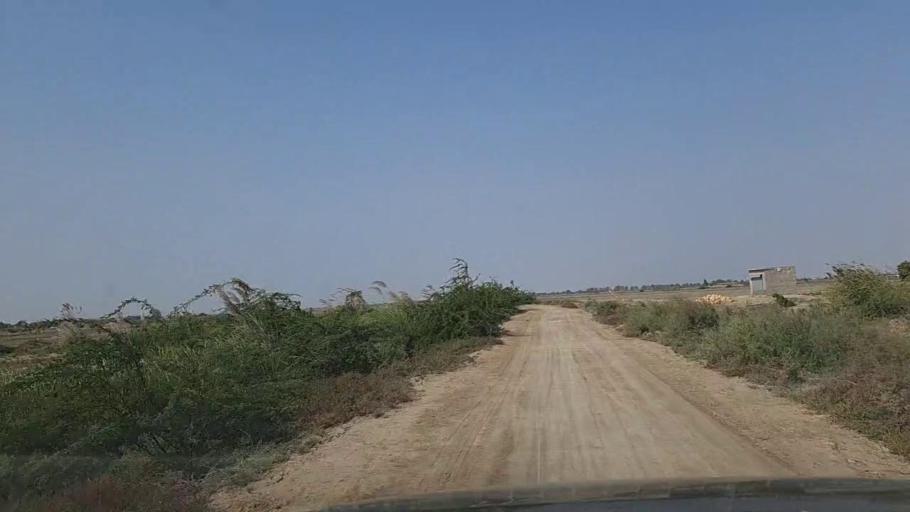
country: PK
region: Sindh
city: Gharo
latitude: 24.7041
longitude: 67.5823
